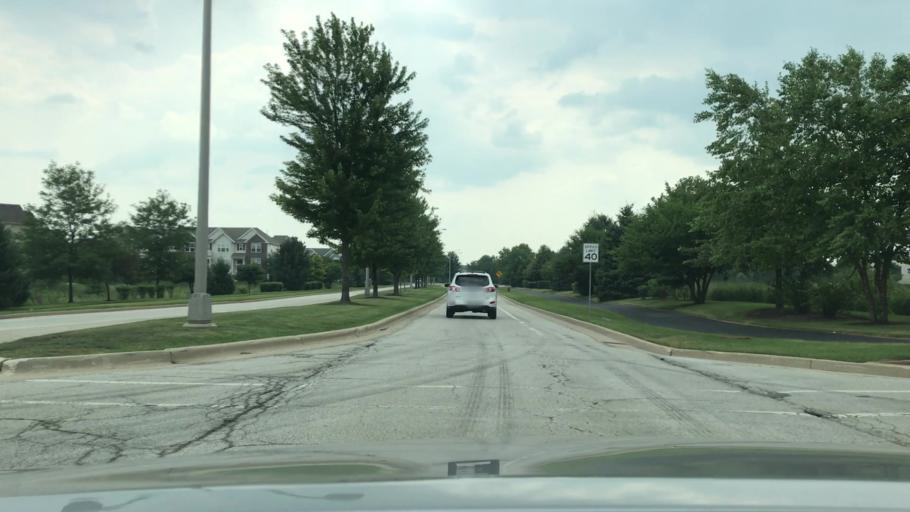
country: US
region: Illinois
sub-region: Will County
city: Plainfield
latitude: 41.6178
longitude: -88.2132
